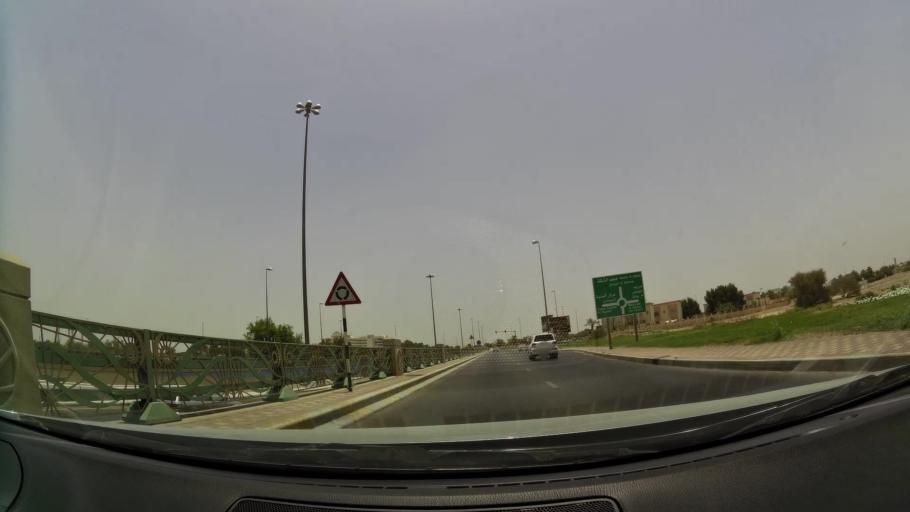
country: AE
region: Abu Dhabi
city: Al Ain
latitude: 24.2057
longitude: 55.7804
